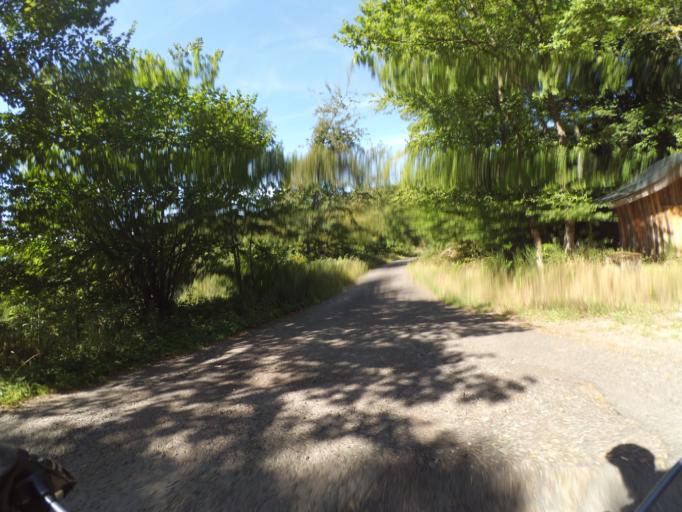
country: DE
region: Rheinland-Pfalz
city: Hilscheid
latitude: 49.7213
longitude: 7.0270
